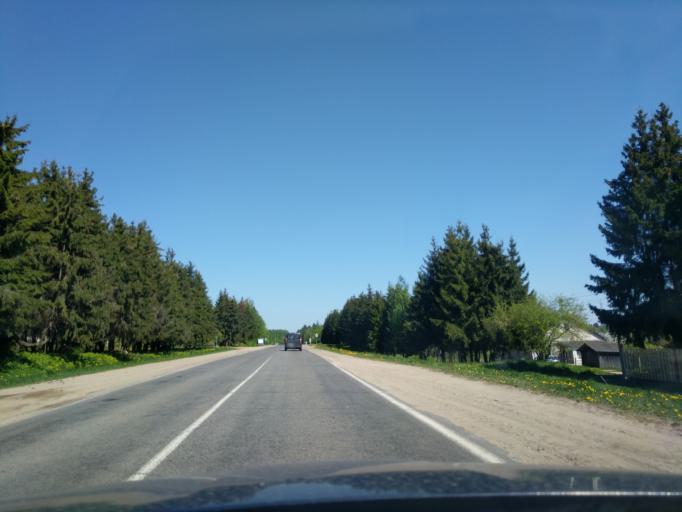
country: BY
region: Minsk
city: Il'ya
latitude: 54.4490
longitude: 27.2851
